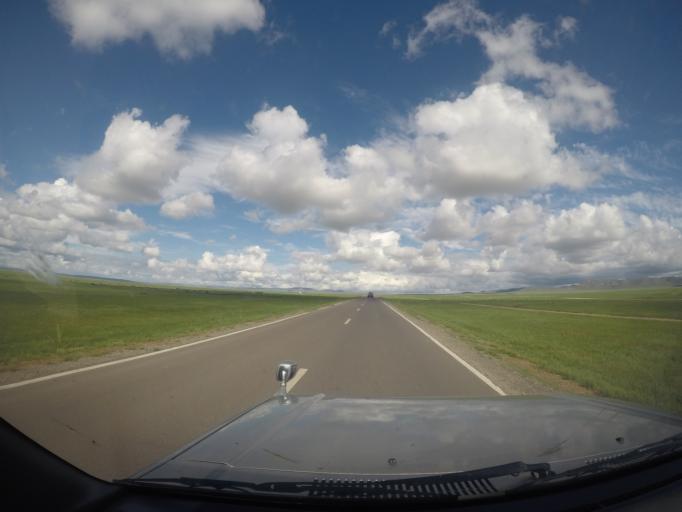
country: MN
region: Hentiy
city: Moron
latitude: 47.4209
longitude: 110.0528
